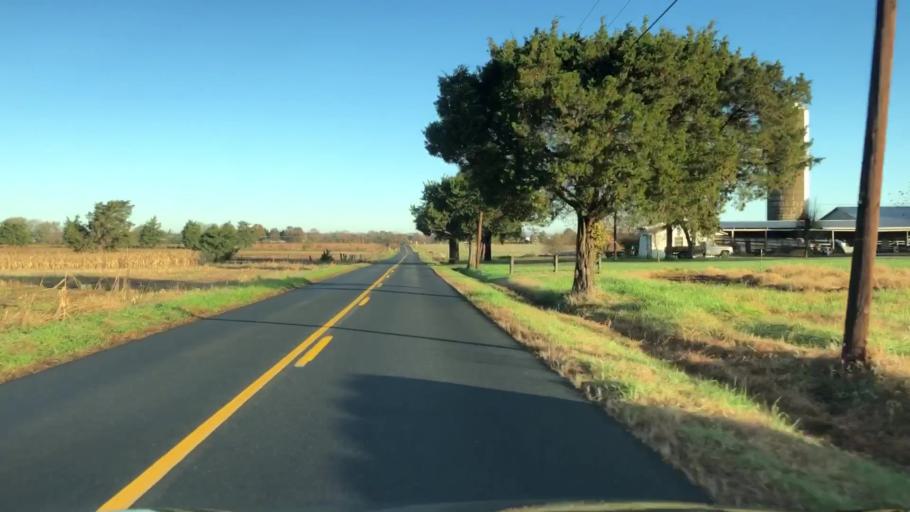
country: US
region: Virginia
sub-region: Prince William County
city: Nokesville
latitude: 38.6430
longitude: -77.6761
